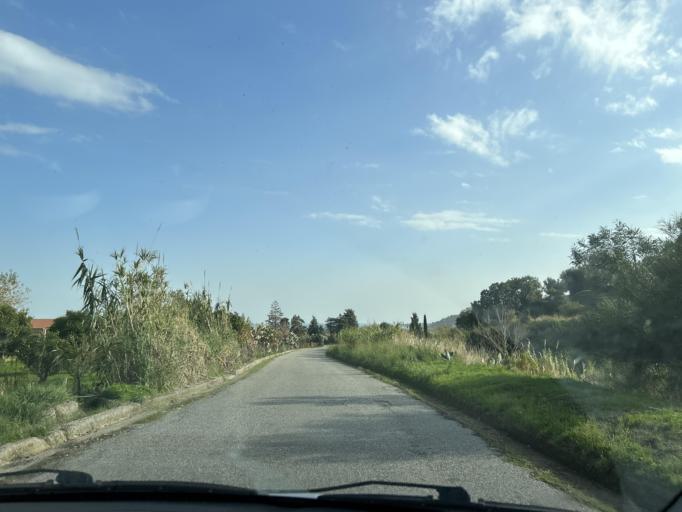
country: IT
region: Calabria
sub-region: Provincia di Catanzaro
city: Montepaone Lido
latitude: 38.7154
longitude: 16.5222
